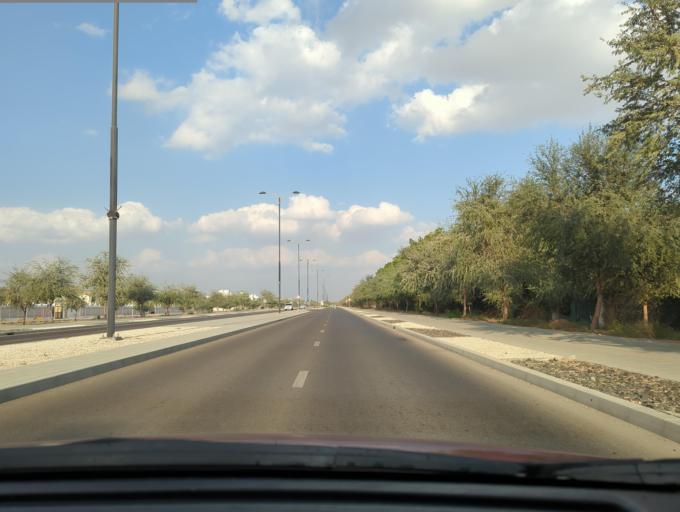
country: AE
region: Abu Dhabi
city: Al Ain
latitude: 24.1554
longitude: 55.6625
